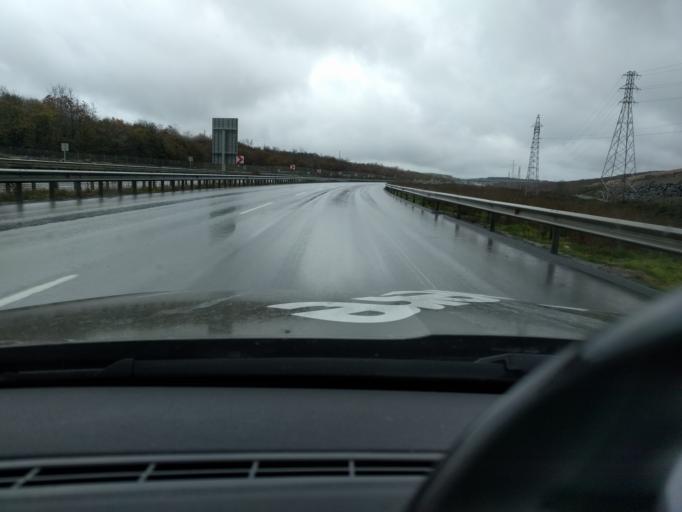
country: TR
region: Istanbul
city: Kemerburgaz
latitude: 41.2139
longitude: 28.8413
